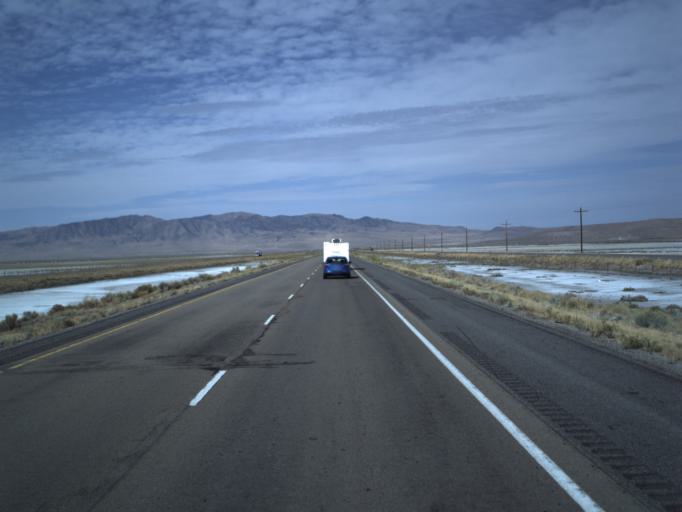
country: US
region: Utah
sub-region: Tooele County
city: Grantsville
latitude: 40.7512
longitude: -112.7035
